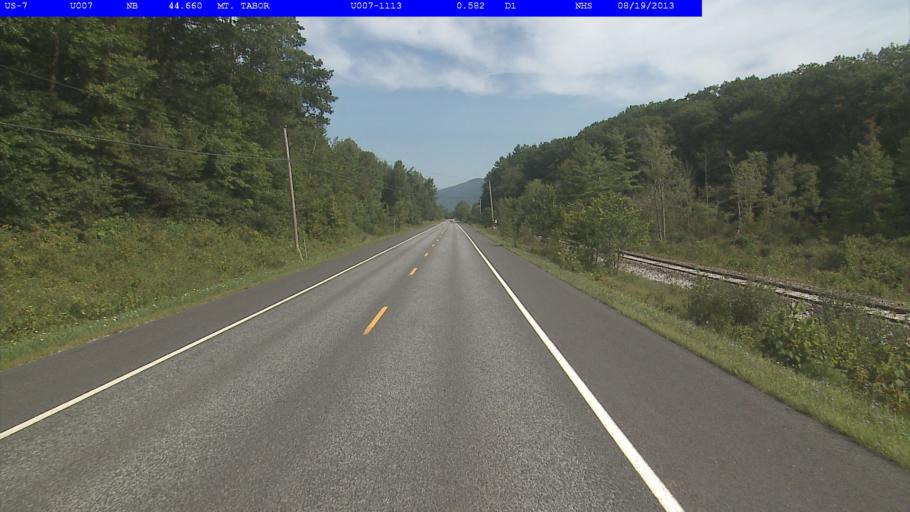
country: US
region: Vermont
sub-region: Bennington County
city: Manchester Center
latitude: 43.3133
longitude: -72.9926
